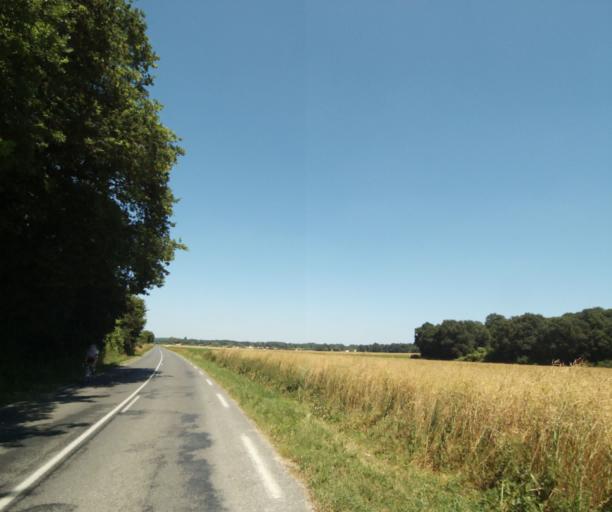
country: FR
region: Ile-de-France
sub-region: Departement de l'Essonne
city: Milly-la-Foret
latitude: 48.3664
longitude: 2.4700
